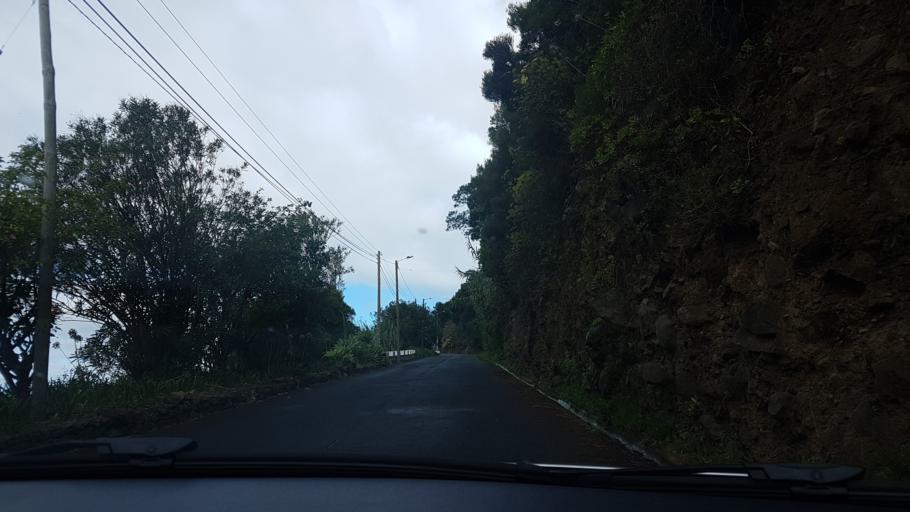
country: PT
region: Madeira
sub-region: Sao Vicente
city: Sao Vicente
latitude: 32.7786
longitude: -17.0306
